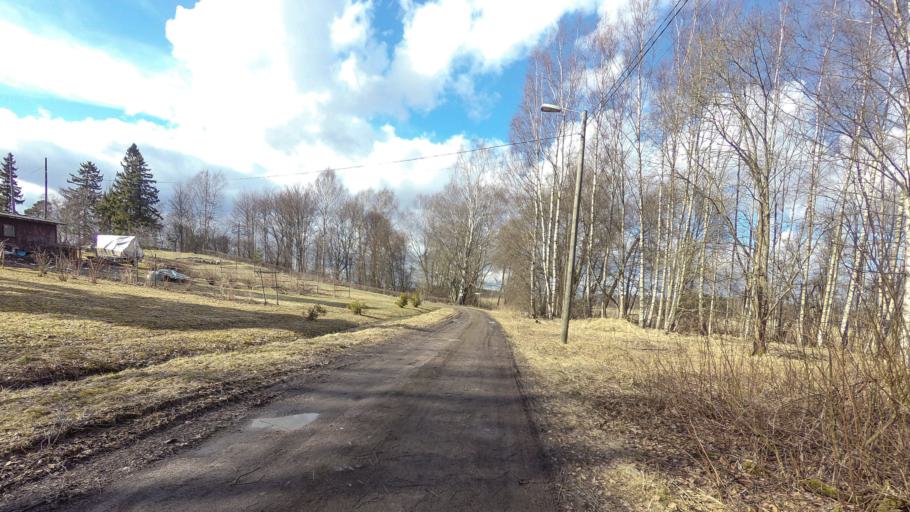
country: FI
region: Uusimaa
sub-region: Helsinki
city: Helsinki
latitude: 60.2049
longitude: 25.0198
